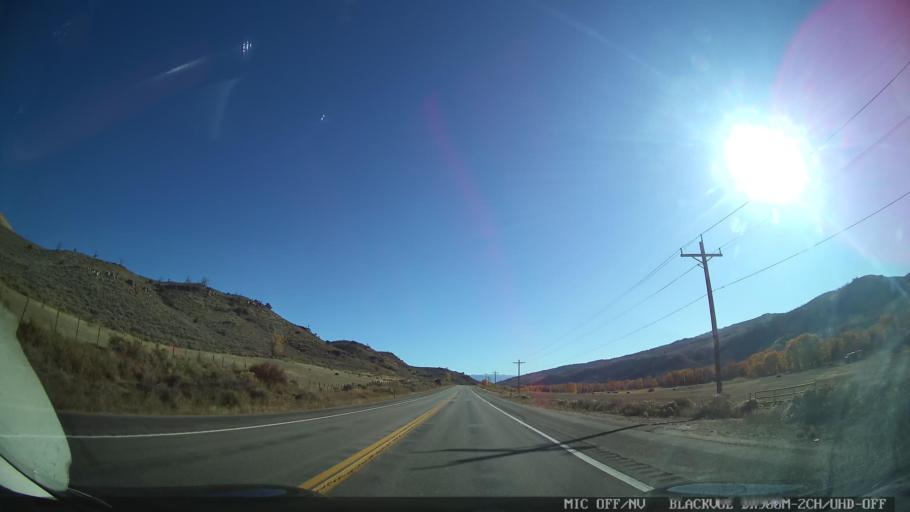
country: US
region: Colorado
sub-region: Grand County
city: Hot Sulphur Springs
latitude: 40.0968
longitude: -106.0537
